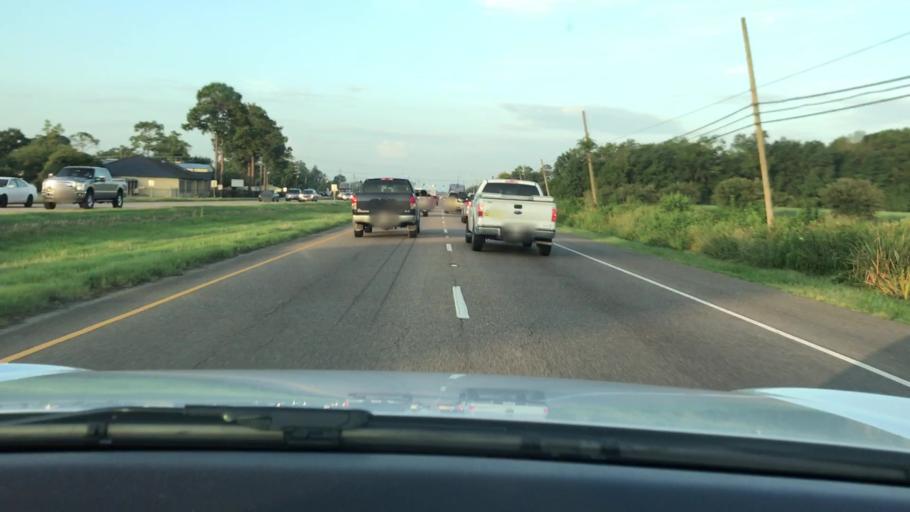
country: US
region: Louisiana
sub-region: West Baton Rouge Parish
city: Brusly
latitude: 30.3836
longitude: -91.2473
